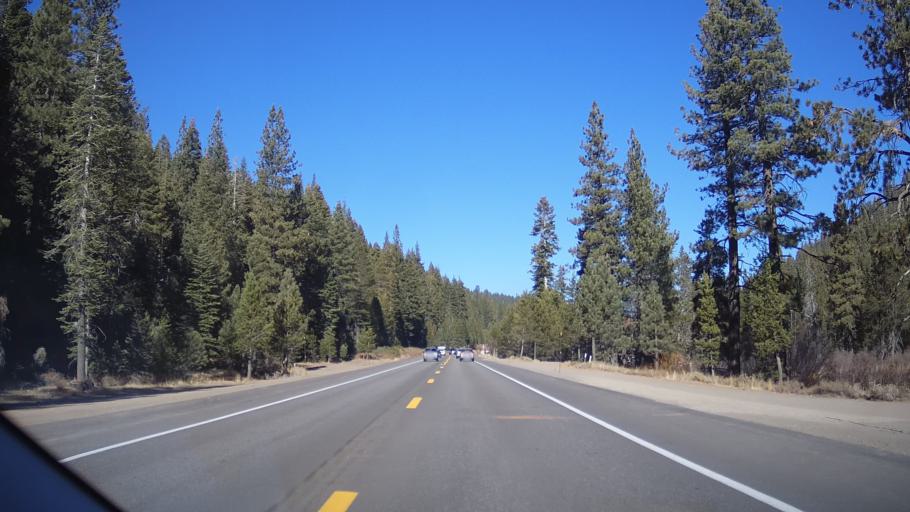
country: US
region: California
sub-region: Nevada County
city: Truckee
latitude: 39.2426
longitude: -120.2101
